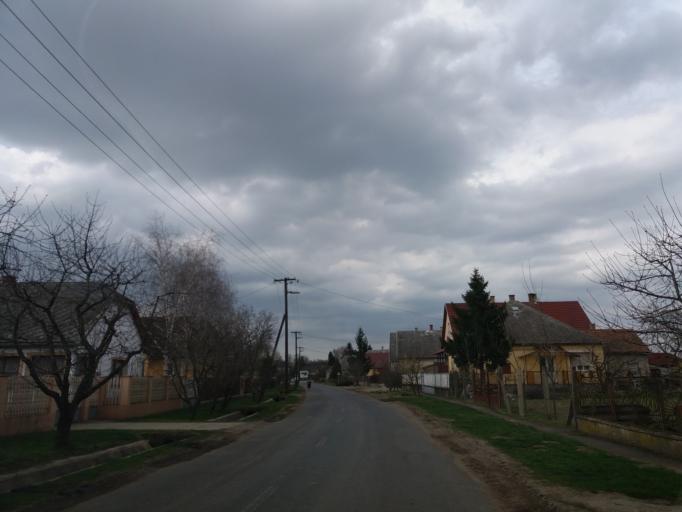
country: HU
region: Szabolcs-Szatmar-Bereg
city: Nyirtass
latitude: 48.1080
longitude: 22.0263
